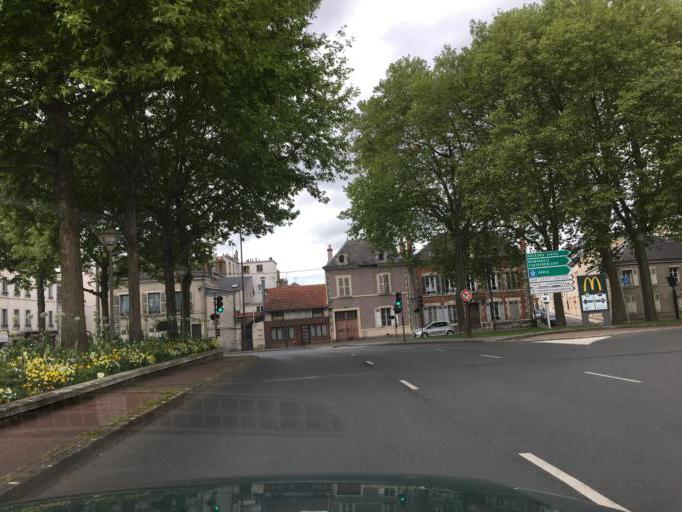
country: FR
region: Centre
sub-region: Departement du Loiret
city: Saint-Jean-le-Blanc
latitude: 47.9012
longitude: 1.9198
